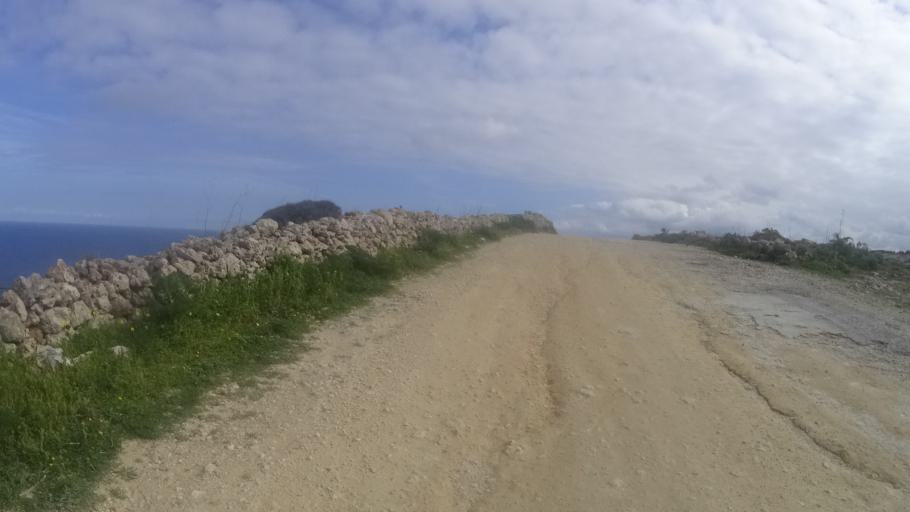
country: MT
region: Il-Qala
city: Qala
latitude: 36.0411
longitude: 14.3199
